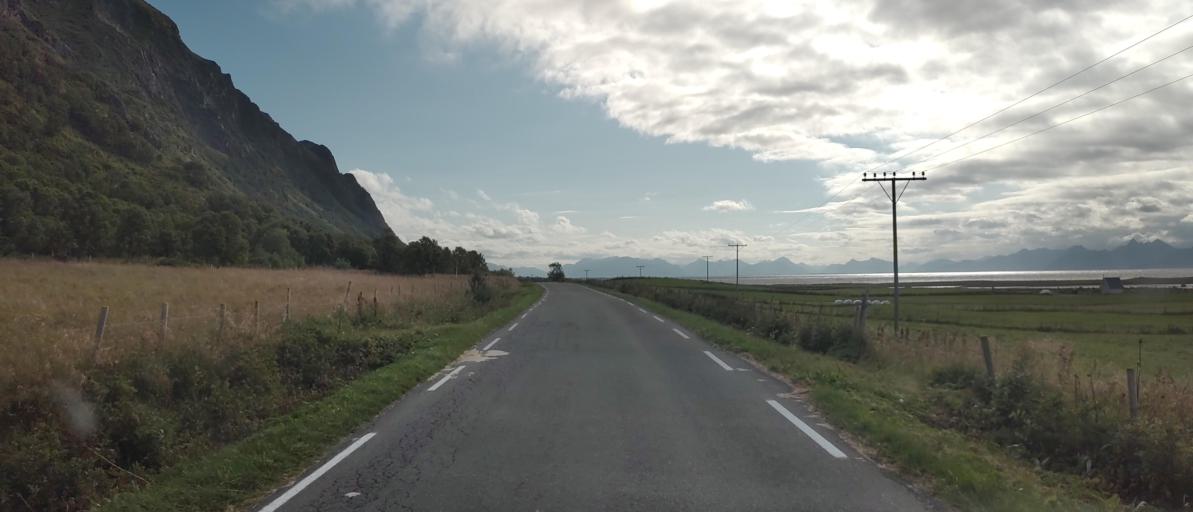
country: NO
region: Nordland
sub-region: Sortland
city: Sortland
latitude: 69.0687
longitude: 15.5423
